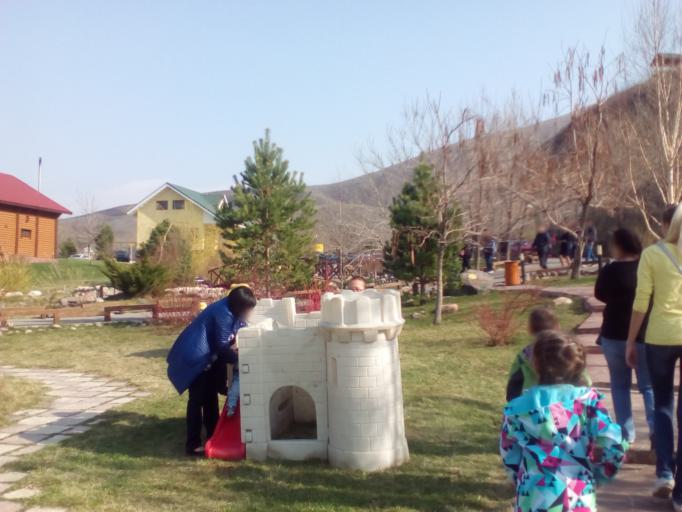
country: KZ
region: Almaty Oblysy
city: Burunday
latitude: 43.1533
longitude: 76.5687
